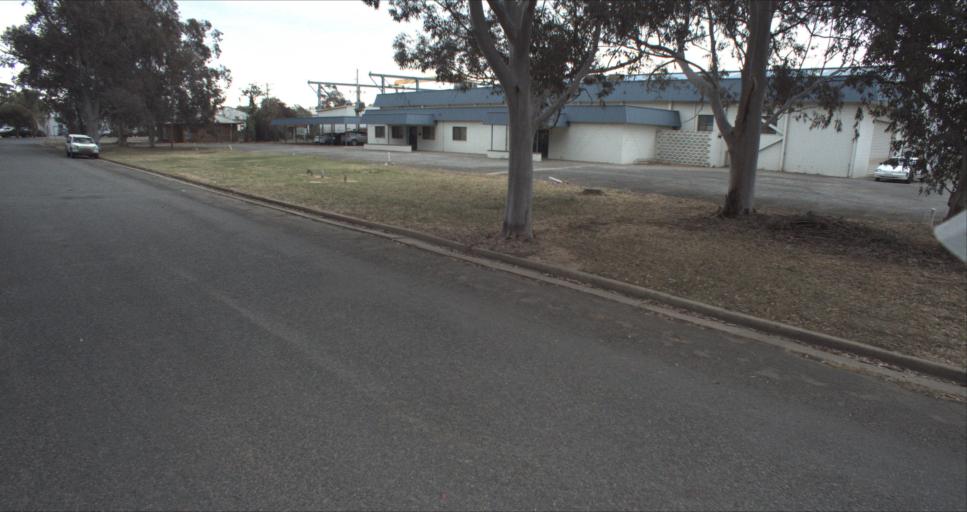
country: AU
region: New South Wales
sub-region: Leeton
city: Leeton
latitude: -34.5508
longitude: 146.3883
